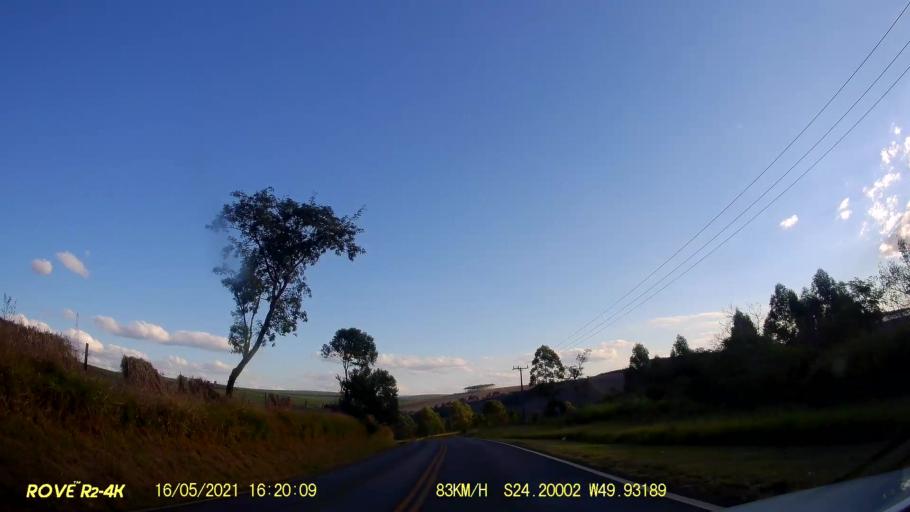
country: BR
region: Parana
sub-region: Jaguariaiva
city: Jaguariaiva
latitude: -24.2002
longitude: -49.9320
